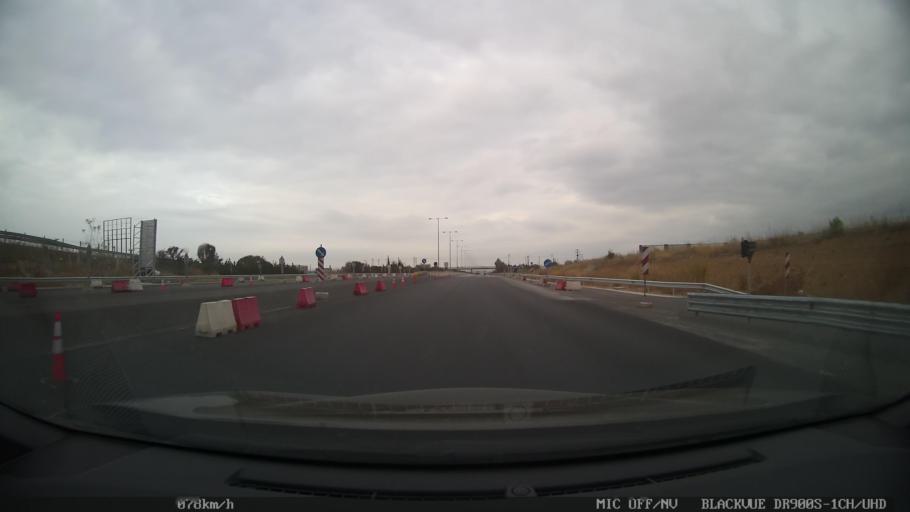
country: GR
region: Central Macedonia
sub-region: Nomos Thessalonikis
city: Evosmos
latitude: 40.6963
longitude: 22.8936
